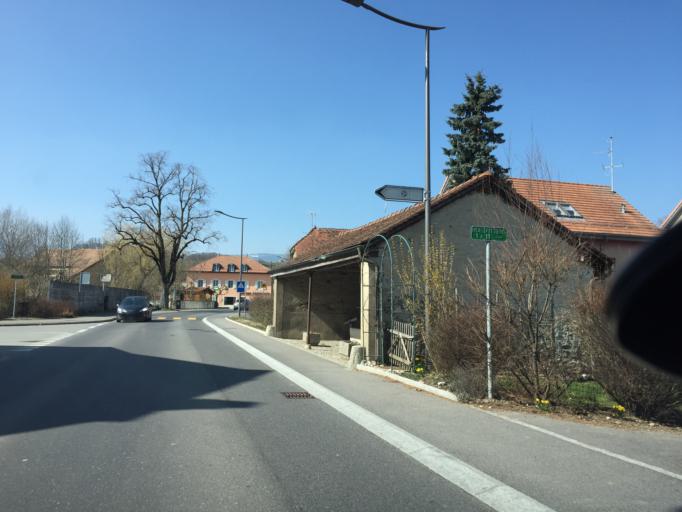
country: CH
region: Vaud
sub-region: Morges District
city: La Chaux
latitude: 46.6150
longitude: 6.4736
